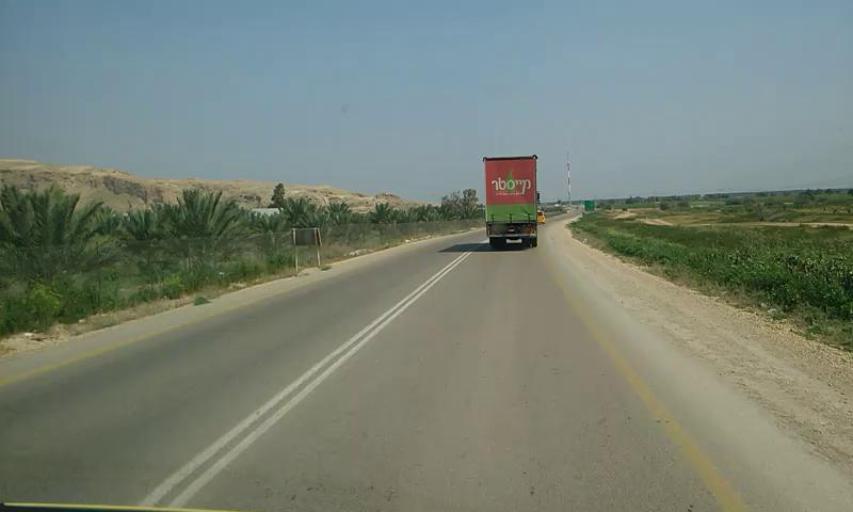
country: PS
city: Al Jiftlik
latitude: 32.1223
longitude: 35.5052
